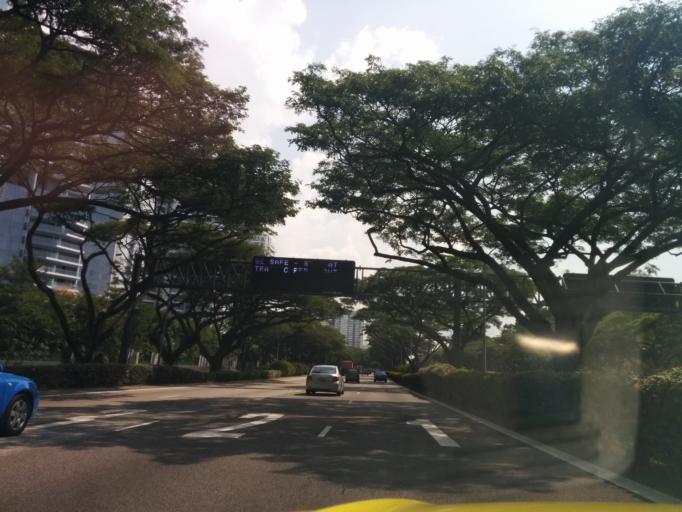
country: SG
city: Singapore
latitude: 1.2989
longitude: 103.9022
